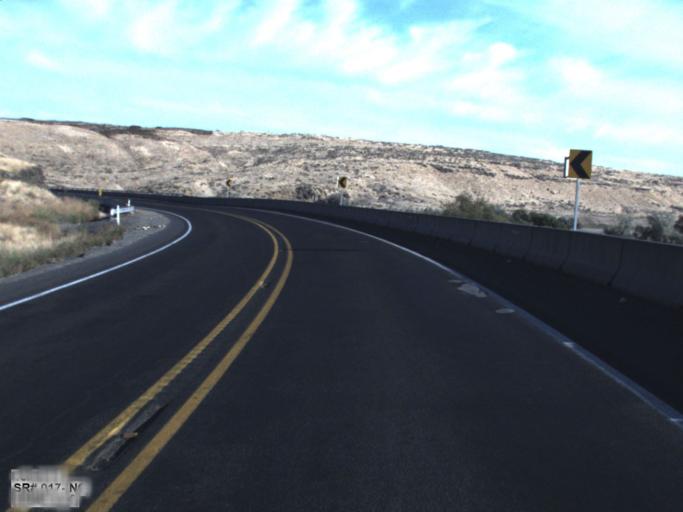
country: US
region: Washington
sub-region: Franklin County
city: Basin City
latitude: 46.5846
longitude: -119.0018
